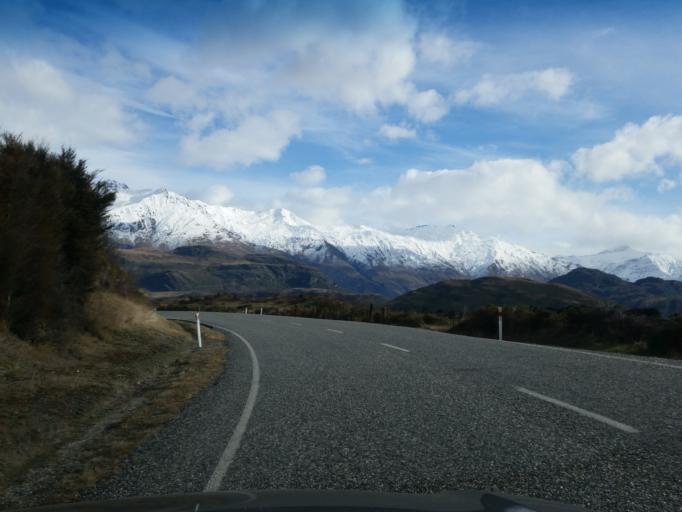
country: NZ
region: Otago
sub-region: Queenstown-Lakes District
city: Wanaka
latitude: -44.6641
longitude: 169.0420
